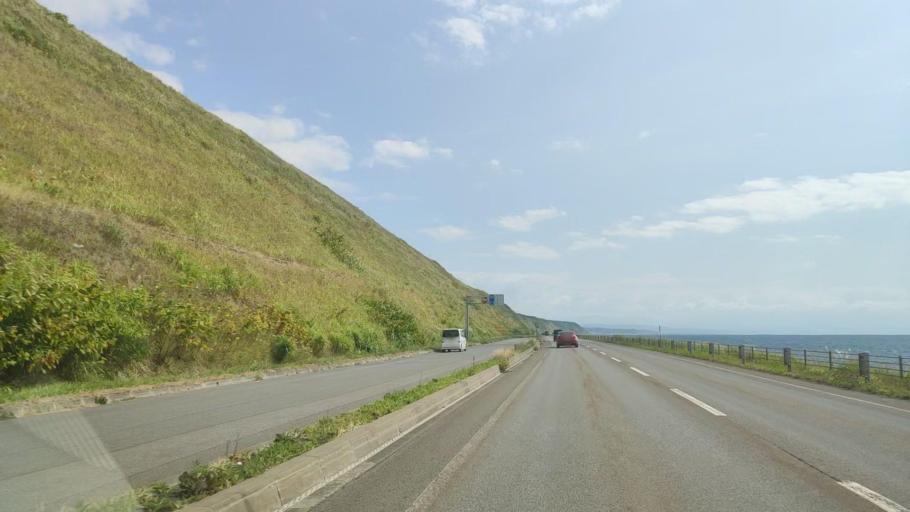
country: JP
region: Hokkaido
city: Rumoi
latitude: 44.0690
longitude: 141.6629
